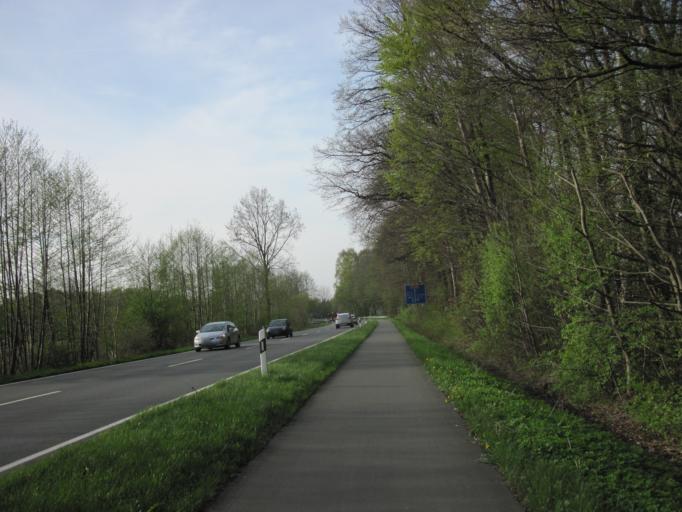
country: DE
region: North Rhine-Westphalia
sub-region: Regierungsbezirk Detmold
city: Hovelhof
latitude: 51.7843
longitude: 8.7075
